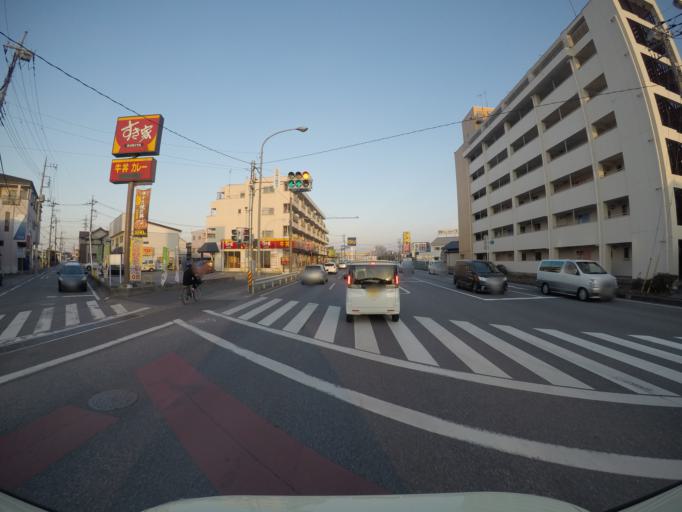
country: JP
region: Tochigi
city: Utsunomiya-shi
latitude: 36.5934
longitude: 139.9251
